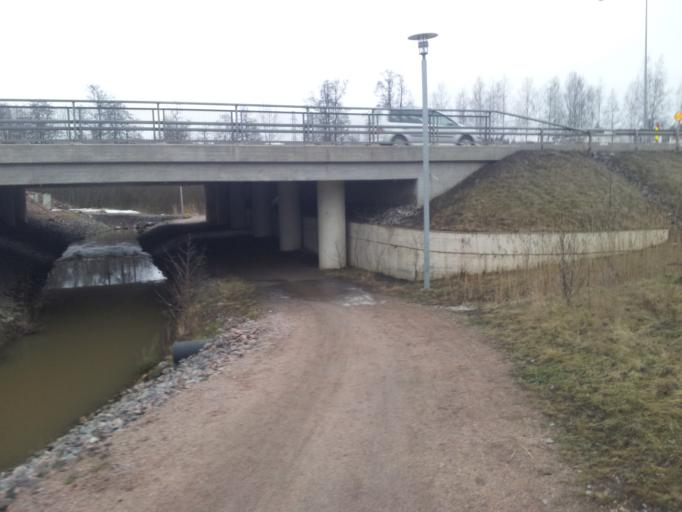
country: FI
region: Uusimaa
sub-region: Helsinki
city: Koukkuniemi
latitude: 60.1615
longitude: 24.7159
